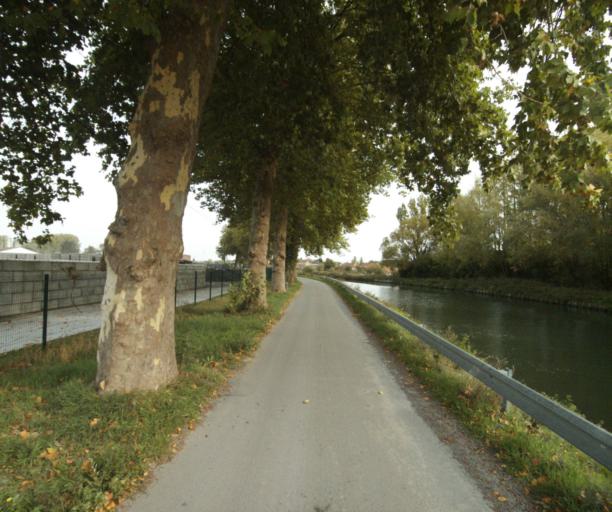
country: FR
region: Nord-Pas-de-Calais
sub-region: Departement du Nord
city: Don
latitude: 50.5464
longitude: 2.9110
